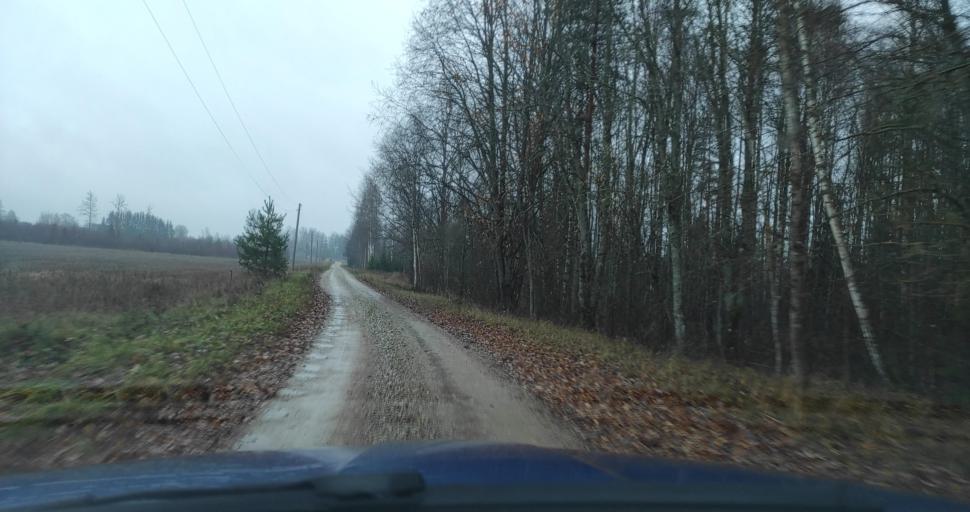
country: LV
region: Alsunga
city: Alsunga
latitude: 56.8880
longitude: 21.5907
